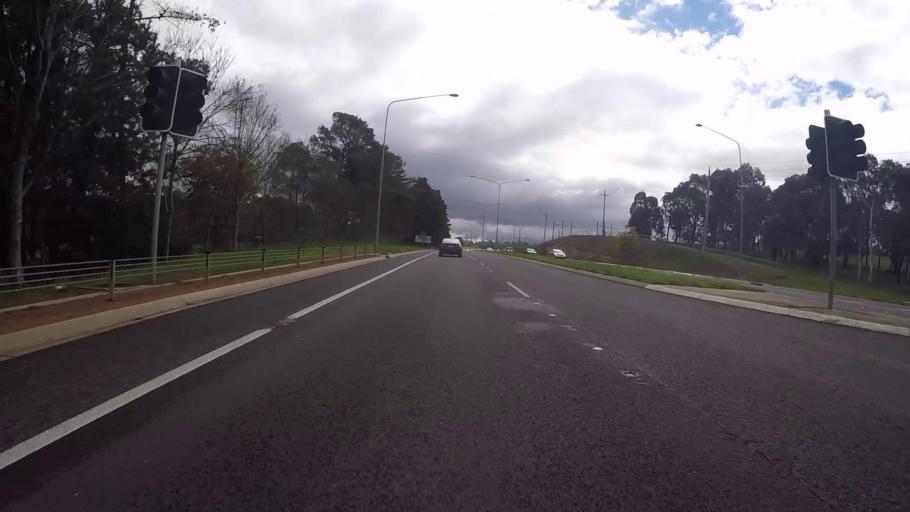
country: AU
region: Australian Capital Territory
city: Kaleen
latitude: -35.2355
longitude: 149.1300
